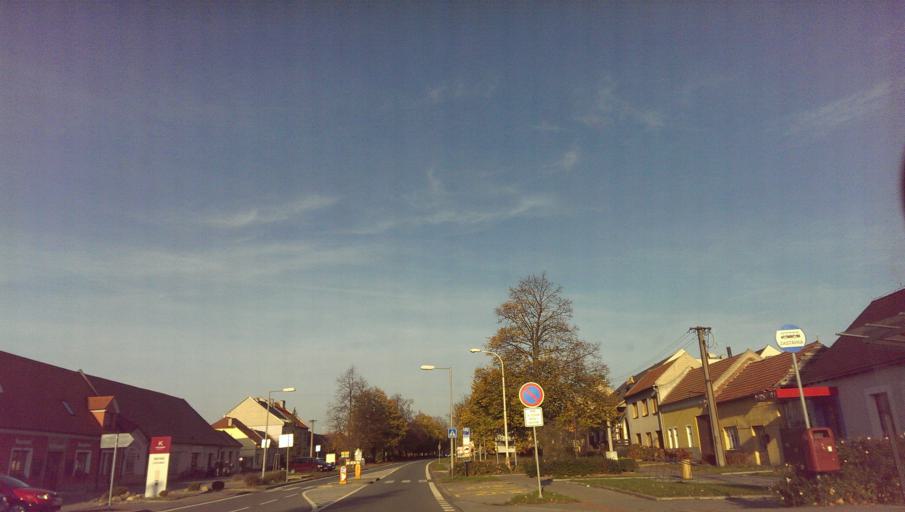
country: CZ
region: Zlin
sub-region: Okres Zlin
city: Ostrozska Nova Ves
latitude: 49.0051
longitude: 17.4349
